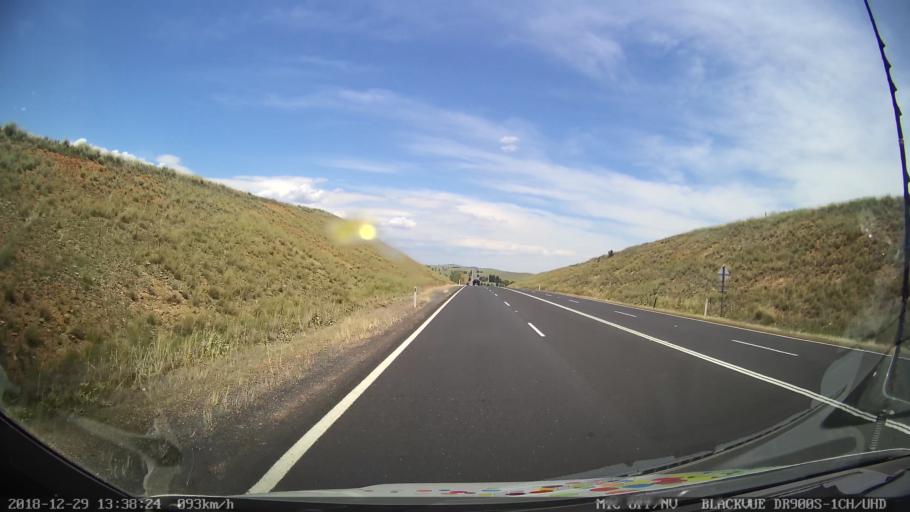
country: AU
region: New South Wales
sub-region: Cooma-Monaro
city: Cooma
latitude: -35.9979
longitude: 149.1413
